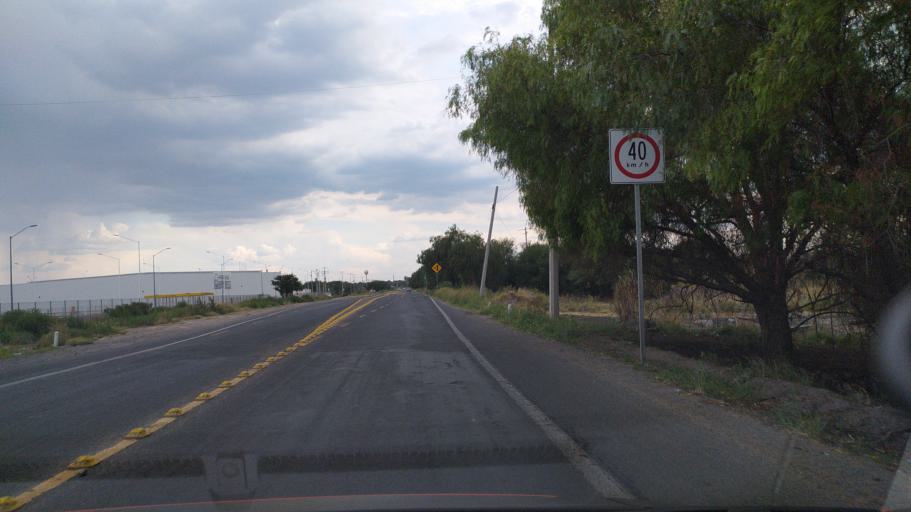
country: MX
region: Guanajuato
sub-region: San Francisco del Rincon
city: Fraccionamiento la Mezquitera
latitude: 21.0052
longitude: -101.8308
